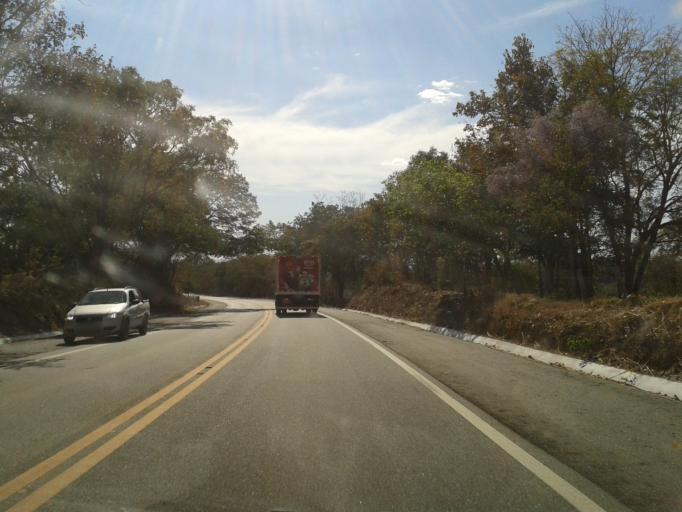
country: BR
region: Goias
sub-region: Goias
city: Goias
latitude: -15.8418
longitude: -50.1053
